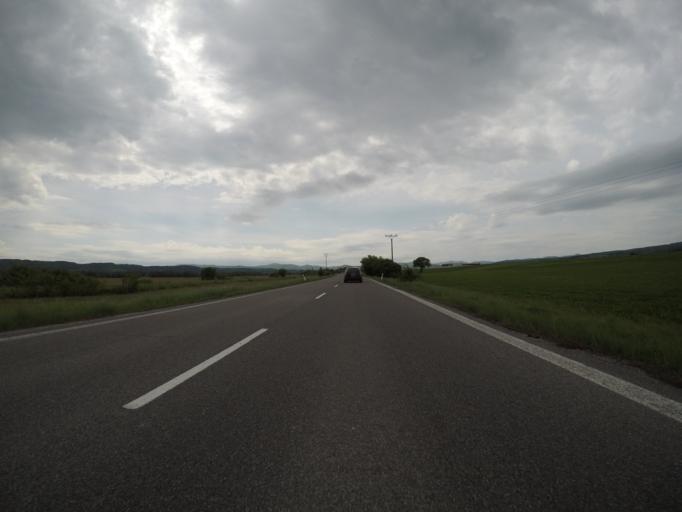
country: SK
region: Banskobystricky
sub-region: Okres Banska Bystrica
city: Zvolen
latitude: 48.6496
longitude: 19.1425
